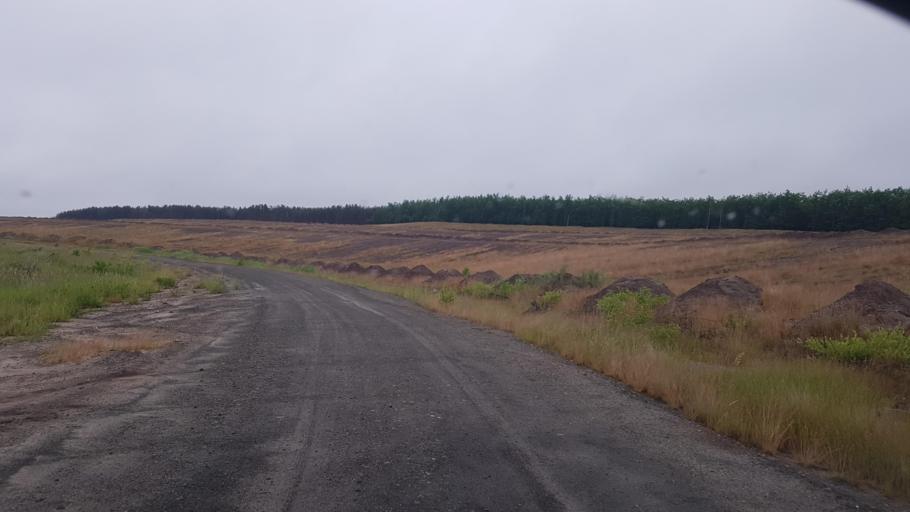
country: DE
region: Brandenburg
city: Lauchhammer
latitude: 51.5340
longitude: 13.7410
